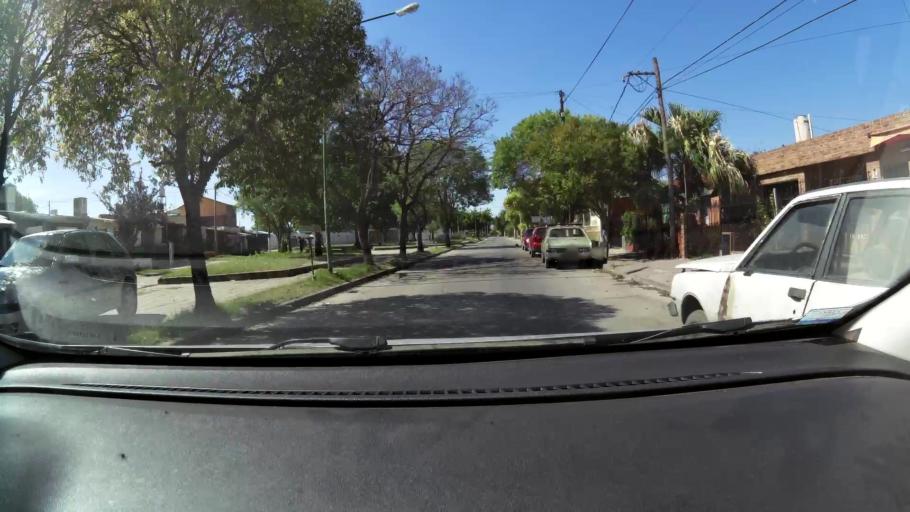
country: AR
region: Cordoba
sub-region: Departamento de Capital
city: Cordoba
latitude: -31.3730
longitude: -64.1560
